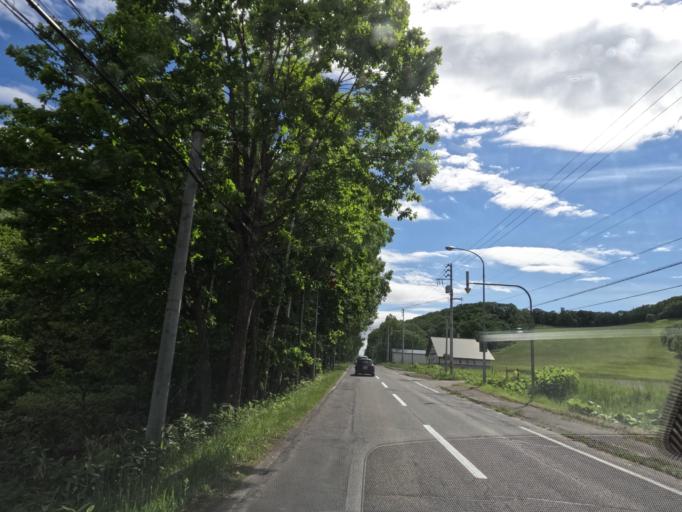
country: JP
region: Hokkaido
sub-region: Asahikawa-shi
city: Asahikawa
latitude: 43.8370
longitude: 142.5398
